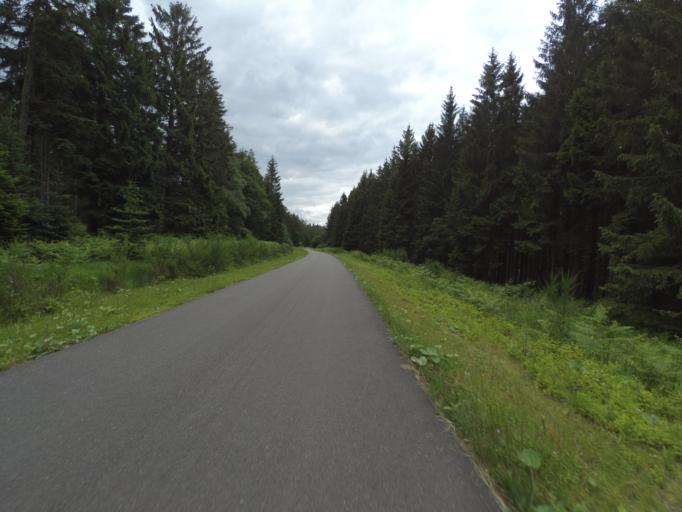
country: DE
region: North Rhine-Westphalia
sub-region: Regierungsbezirk Koln
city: Roetgen
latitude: 50.6460
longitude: 6.2258
